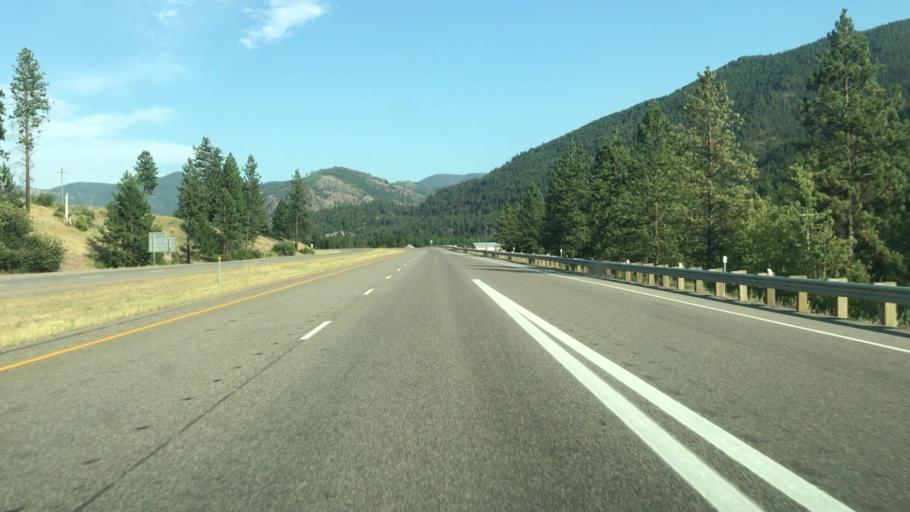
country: US
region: Montana
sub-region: Missoula County
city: Frenchtown
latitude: 47.0038
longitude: -114.4903
